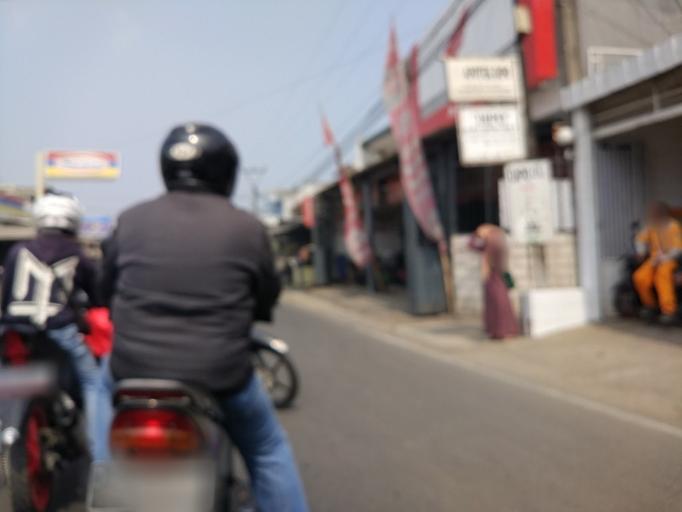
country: ID
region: West Java
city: Padalarang
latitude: -6.8444
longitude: 107.4981
